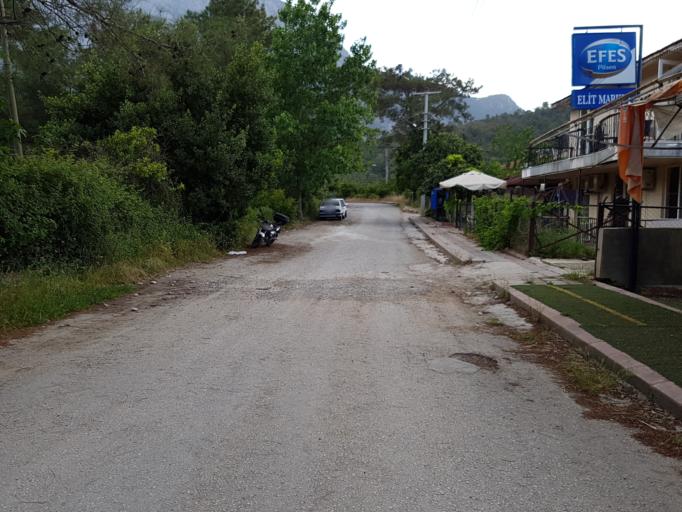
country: TR
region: Antalya
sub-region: Kemer
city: Goeynuek
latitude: 36.6433
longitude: 30.5516
